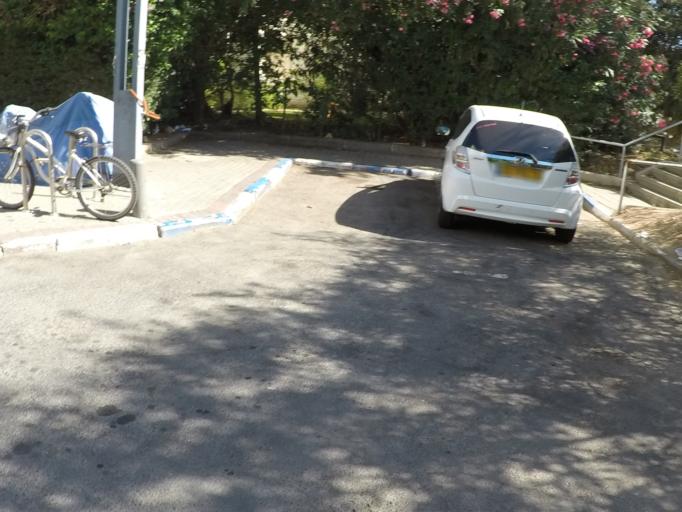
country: IL
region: Tel Aviv
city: Tel Aviv
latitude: 32.1109
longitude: 34.7928
